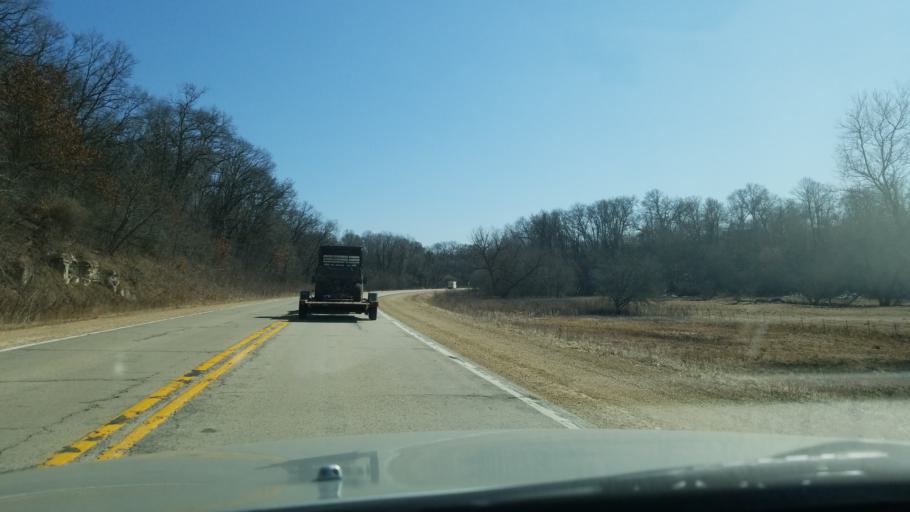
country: US
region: Wisconsin
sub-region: Iowa County
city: Mineral Point
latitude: 42.8739
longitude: -90.2062
